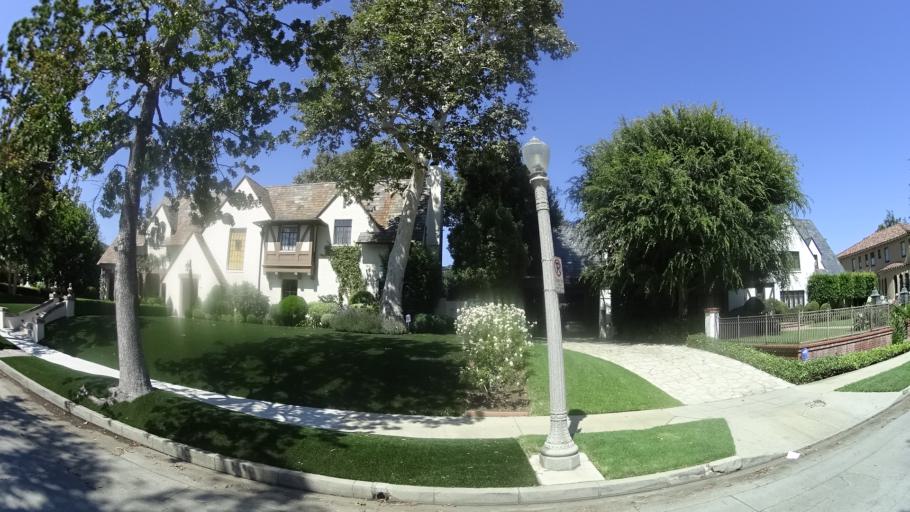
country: US
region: California
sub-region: Los Angeles County
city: Hollywood
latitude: 34.0730
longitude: -118.3319
